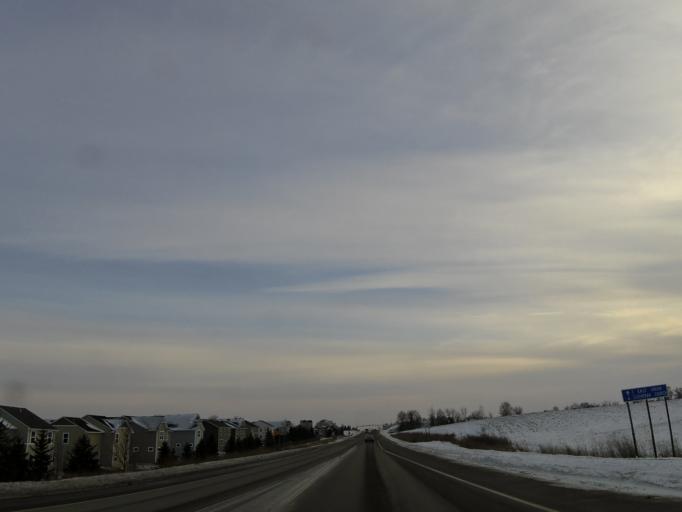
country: US
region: Minnesota
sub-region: Carver County
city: Carver
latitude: 44.7751
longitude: -93.6426
